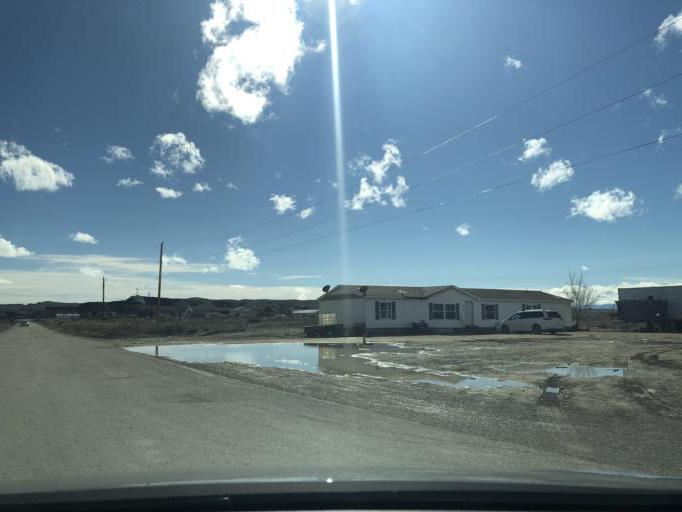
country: US
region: Utah
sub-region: Carbon County
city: East Carbon City
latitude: 39.0006
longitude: -110.1652
